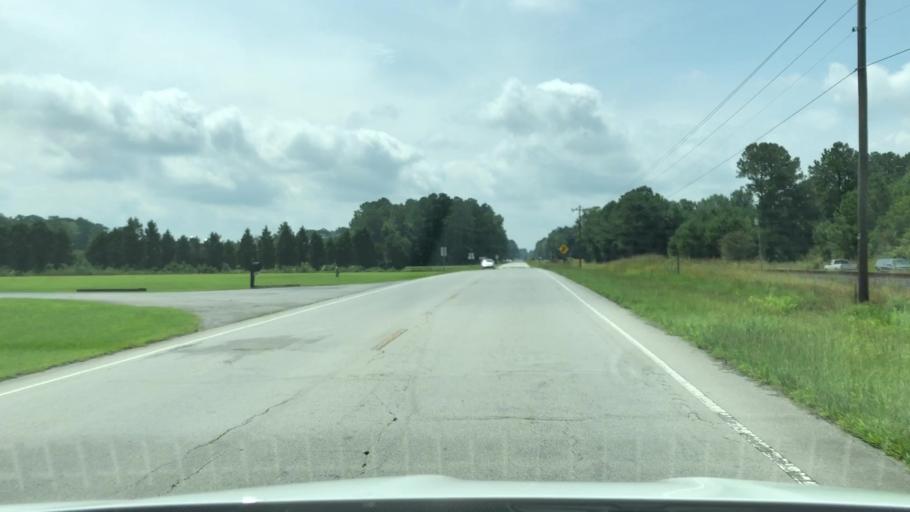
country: US
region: North Carolina
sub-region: Craven County
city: Vanceboro
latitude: 35.3430
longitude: -77.1510
